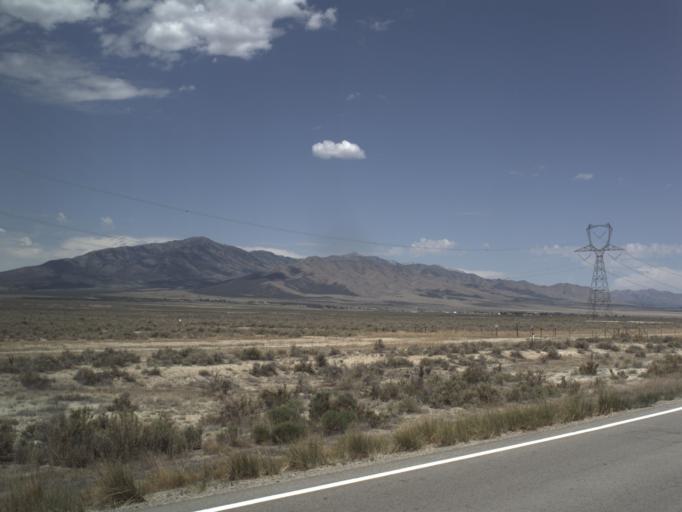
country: US
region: Utah
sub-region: Tooele County
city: Tooele
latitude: 40.2913
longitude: -112.4007
